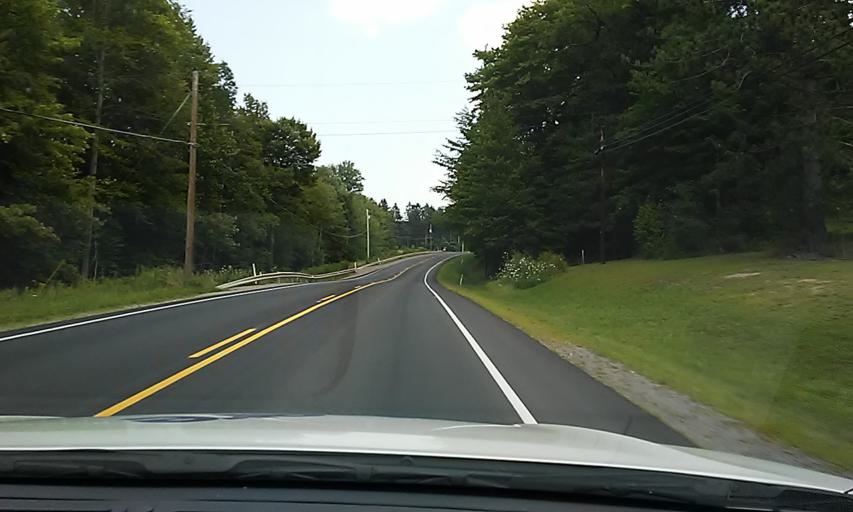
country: US
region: Pennsylvania
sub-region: Elk County
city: Saint Marys
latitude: 41.4470
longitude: -78.4691
